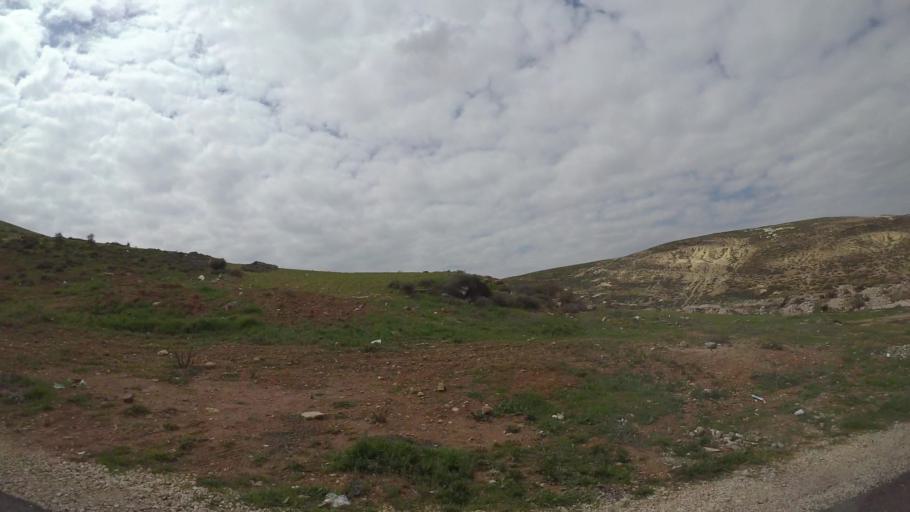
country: JO
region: Amman
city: Al Jubayhah
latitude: 32.0048
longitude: 35.9109
